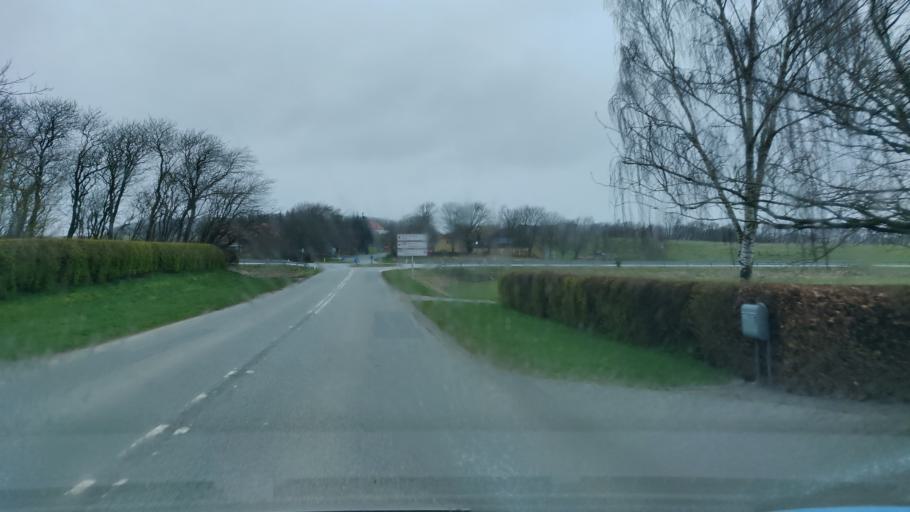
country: DK
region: Central Jutland
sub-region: Skive Kommune
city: Hojslev
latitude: 56.5903
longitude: 9.2213
